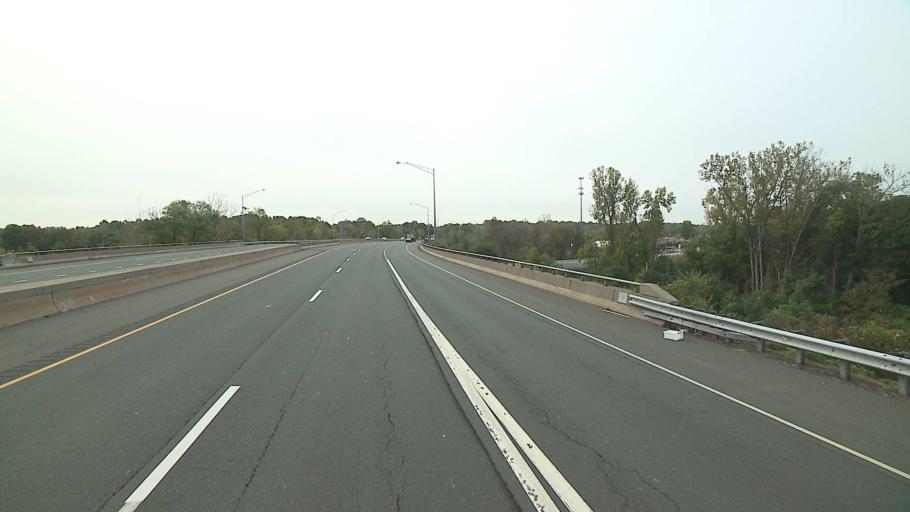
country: US
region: Connecticut
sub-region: Hartford County
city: Newington
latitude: 41.6901
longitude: -72.7572
